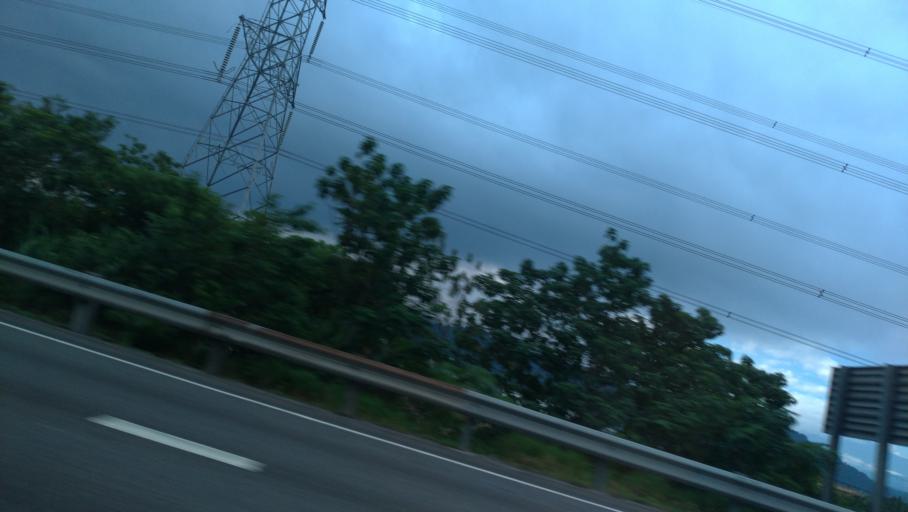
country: TW
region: Taiwan
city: Daxi
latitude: 24.9256
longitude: 121.3067
